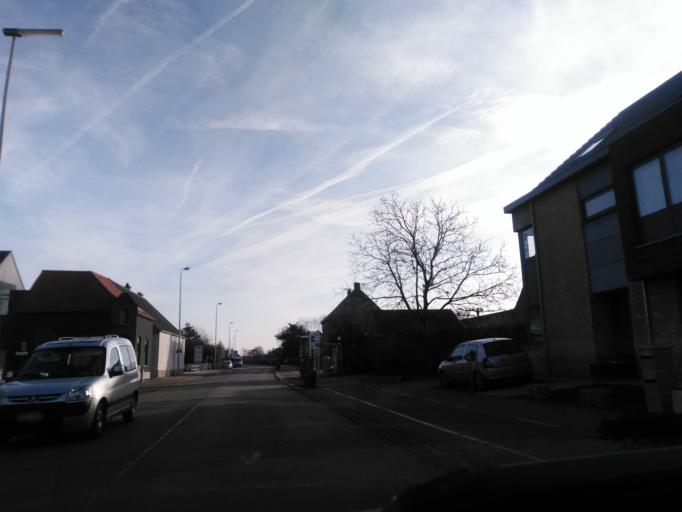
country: BE
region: Flanders
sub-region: Provincie Oost-Vlaanderen
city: Sint-Gillis-Waas
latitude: 51.2117
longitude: 4.1366
